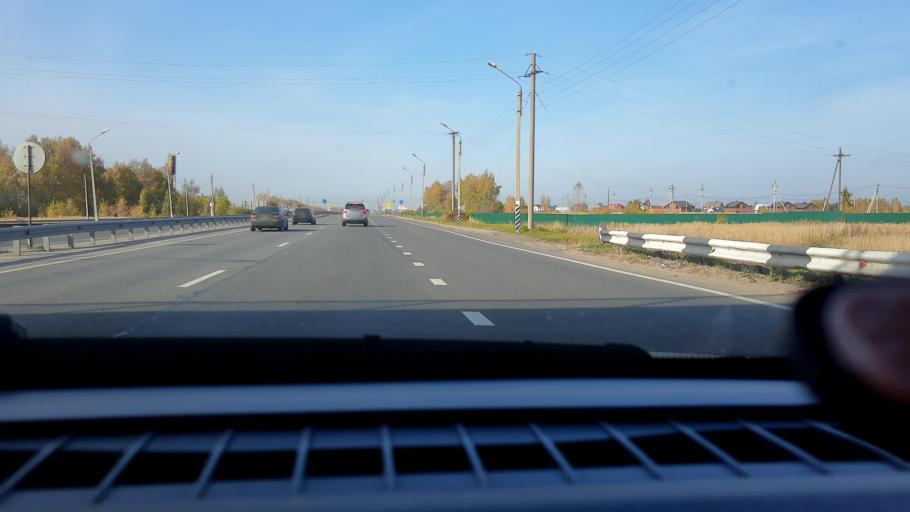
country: RU
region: Nizjnij Novgorod
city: Kstovo
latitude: 56.1279
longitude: 44.2597
